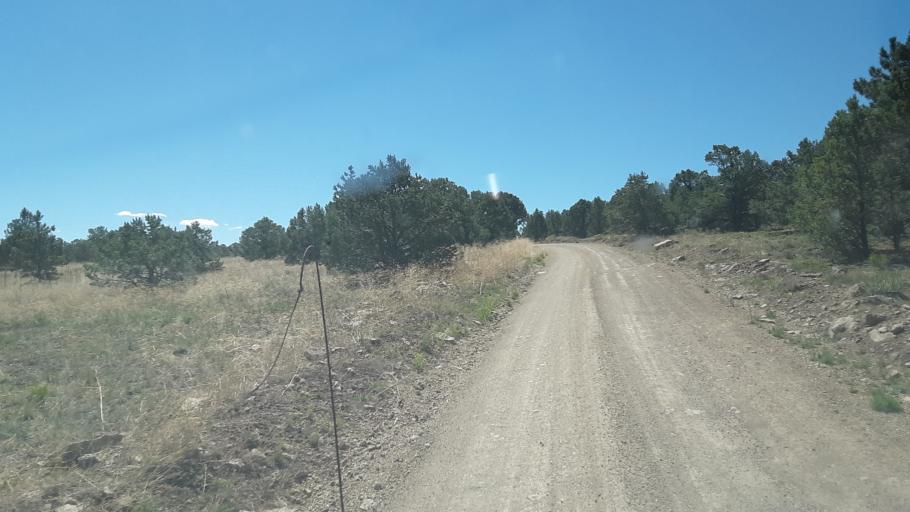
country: US
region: Colorado
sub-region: Custer County
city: Westcliffe
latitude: 38.2523
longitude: -105.5672
